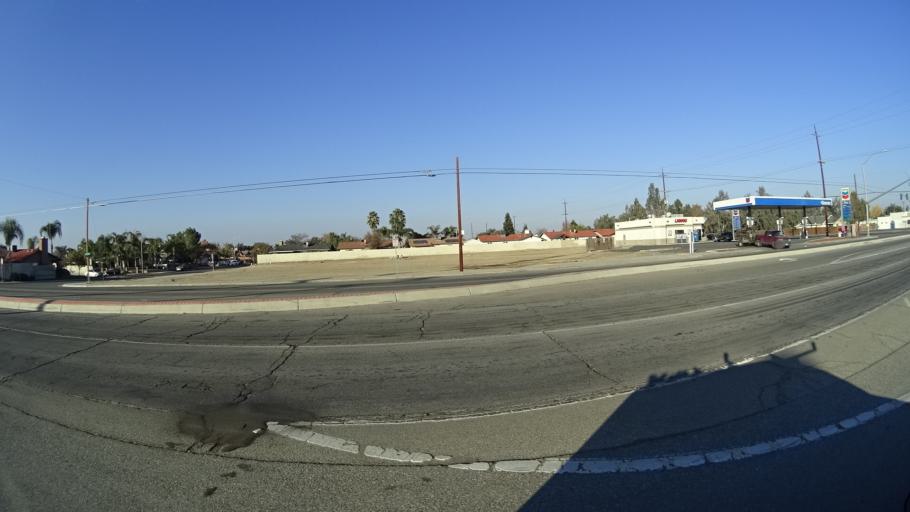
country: US
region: California
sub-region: Kern County
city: Greenfield
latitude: 35.2948
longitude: -119.0030
